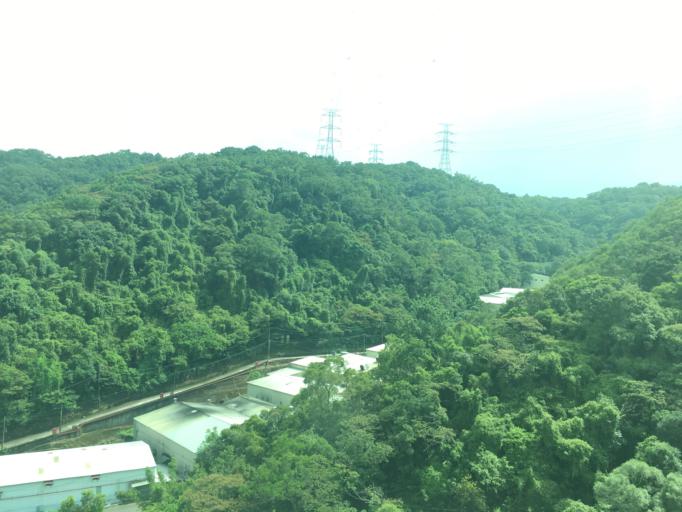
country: TW
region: Taipei
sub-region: Taipei
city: Banqiao
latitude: 25.0323
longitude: 121.3969
